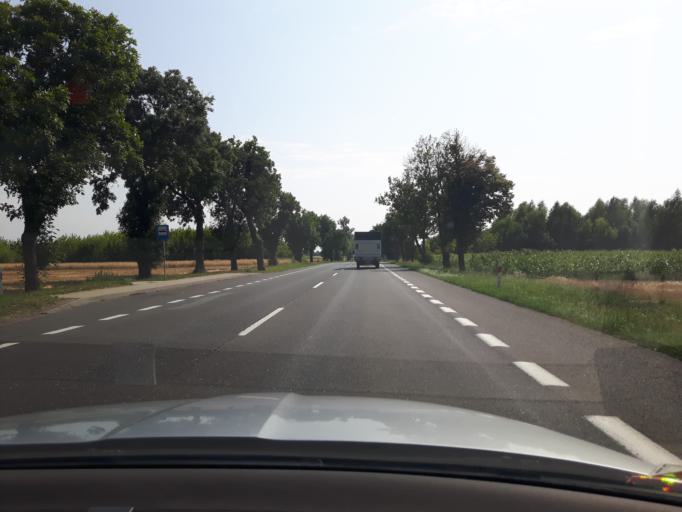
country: PL
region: Masovian Voivodeship
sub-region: Powiat mlawski
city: Wisniewo
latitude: 53.0122
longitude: 20.3318
